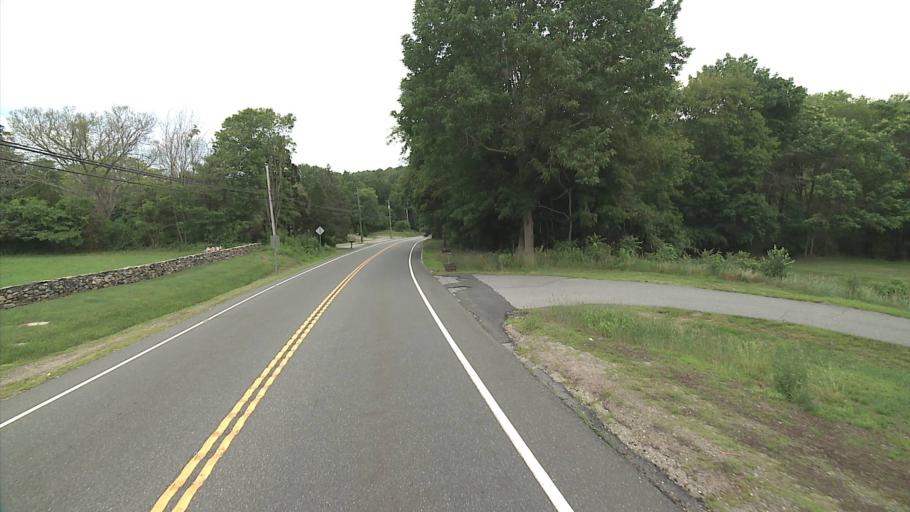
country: US
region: Connecticut
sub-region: New London County
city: Ledyard Center
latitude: 41.4692
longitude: -72.0247
